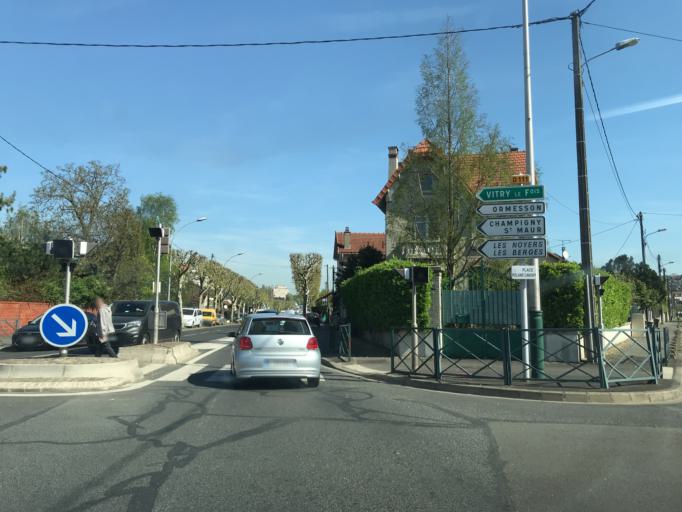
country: FR
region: Ile-de-France
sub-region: Departement du Val-de-Marne
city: Boissy-Saint-Leger
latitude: 48.7747
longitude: 2.5110
